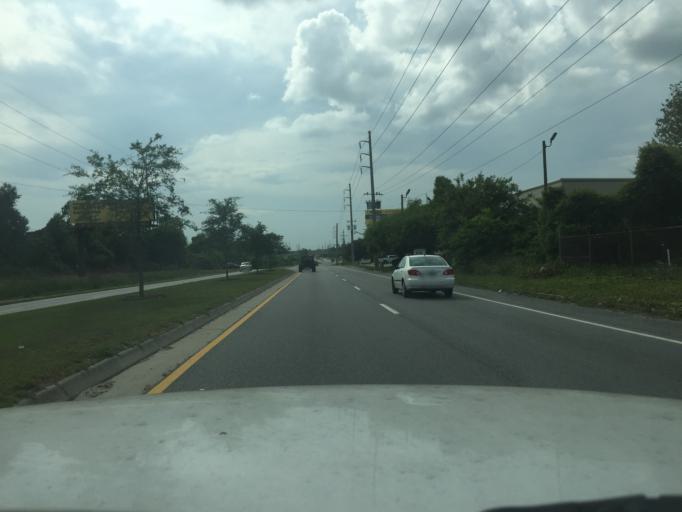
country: US
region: Georgia
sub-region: Chatham County
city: Savannah
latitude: 32.0711
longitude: -81.0626
